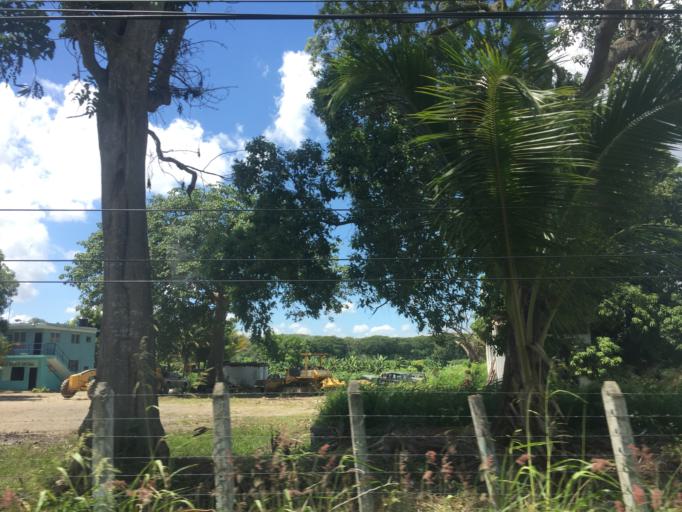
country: DO
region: Santiago
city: Santiago de los Caballeros
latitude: 19.4518
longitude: -70.7514
